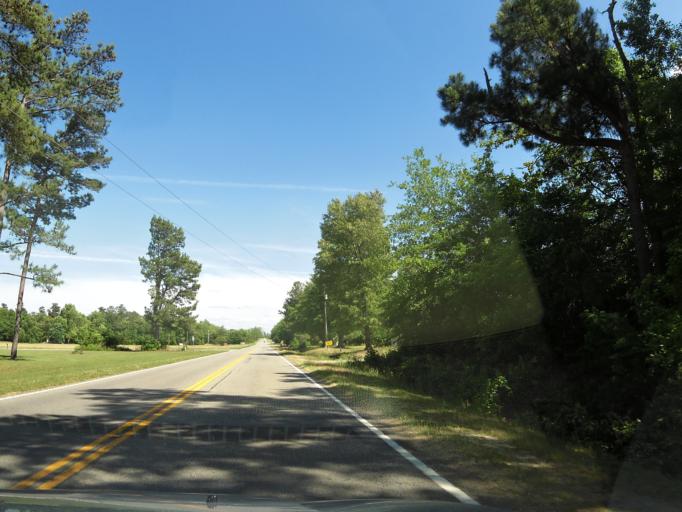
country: US
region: South Carolina
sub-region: Barnwell County
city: Williston
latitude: 33.4117
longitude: -81.4540
